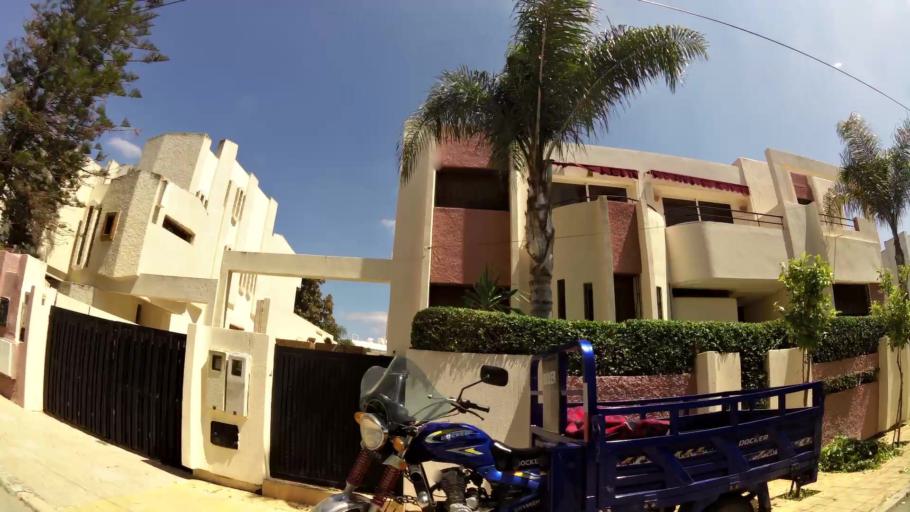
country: MA
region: Fes-Boulemane
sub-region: Fes
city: Fes
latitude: 34.0292
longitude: -5.0130
